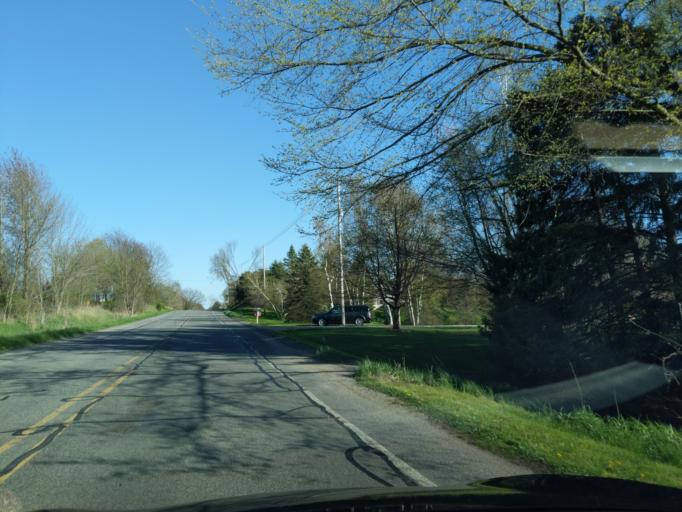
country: US
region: Michigan
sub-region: Ionia County
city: Portland
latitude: 42.8309
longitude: -84.8506
